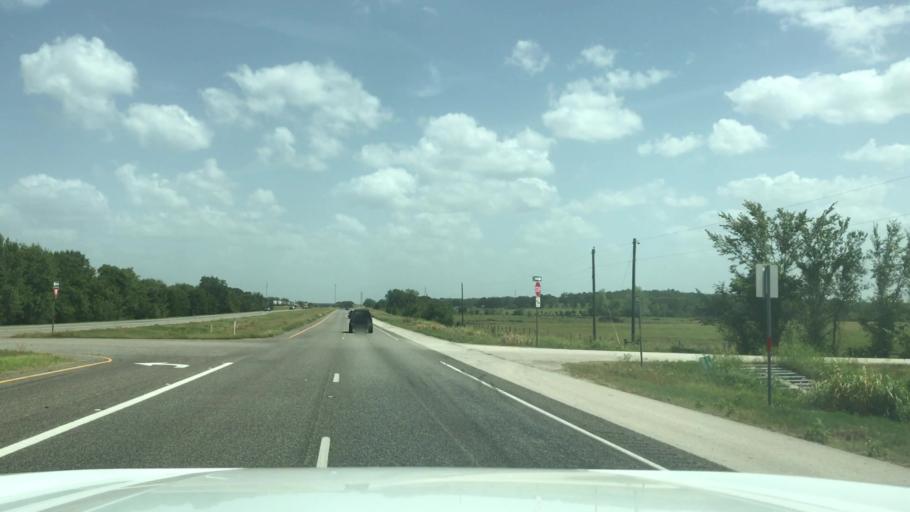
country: US
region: Texas
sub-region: Robertson County
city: Hearne
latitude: 30.9162
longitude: -96.6187
